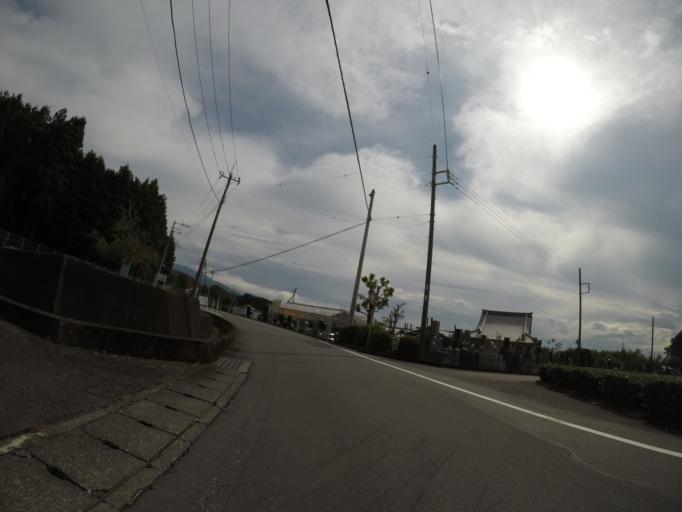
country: JP
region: Shizuoka
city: Fuji
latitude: 35.2269
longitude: 138.6882
